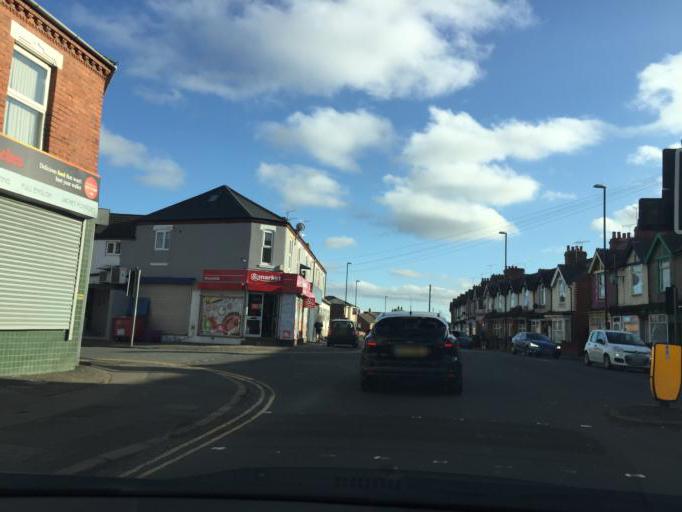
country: GB
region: England
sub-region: Coventry
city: Coventry
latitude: 52.4035
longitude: -1.4868
